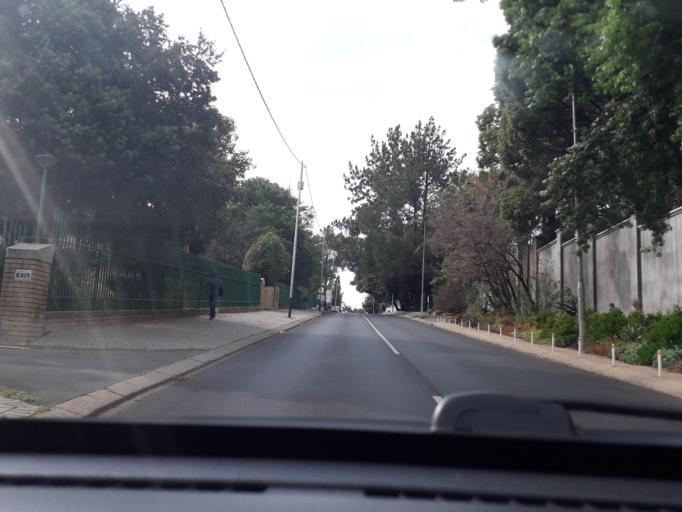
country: ZA
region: Gauteng
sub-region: City of Johannesburg Metropolitan Municipality
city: Johannesburg
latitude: -26.0730
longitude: 28.0108
